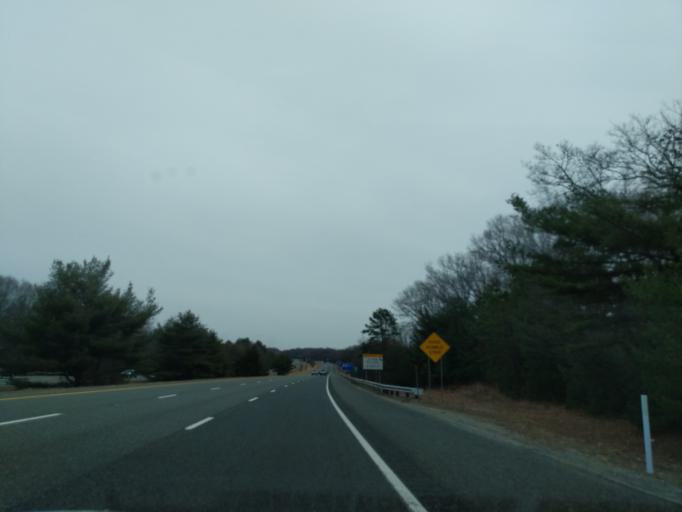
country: US
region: Rhode Island
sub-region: Providence County
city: Valley Falls
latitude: 41.9525
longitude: -71.3787
